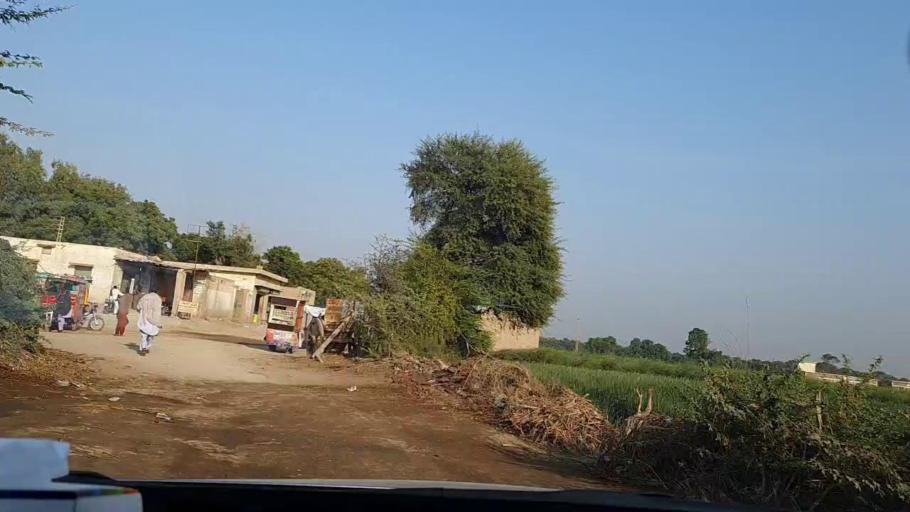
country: PK
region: Sindh
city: Tando Ghulam Ali
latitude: 25.2096
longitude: 68.9008
